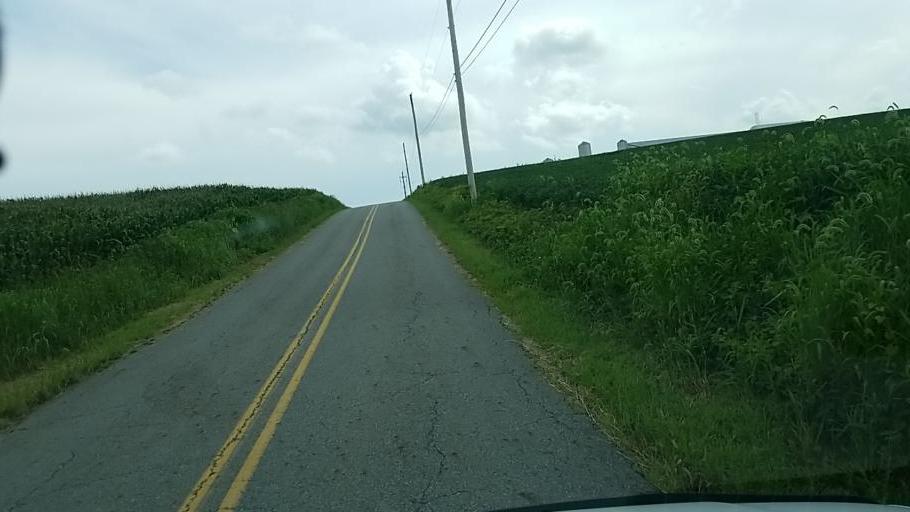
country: US
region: Pennsylvania
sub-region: Dauphin County
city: Elizabethville
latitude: 40.6535
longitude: -76.8351
